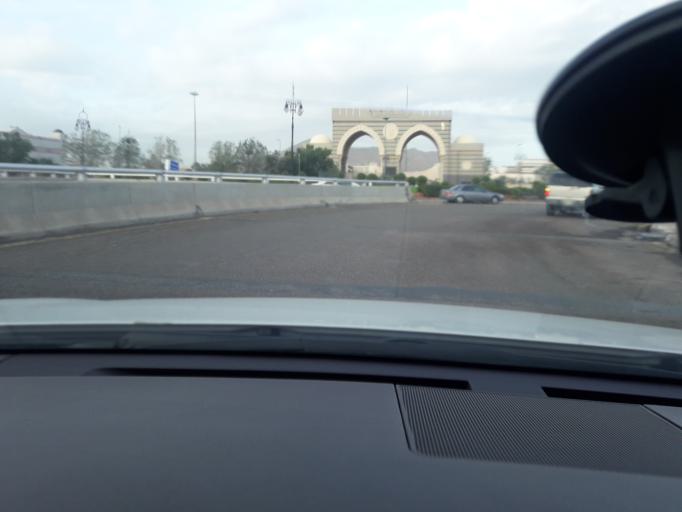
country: SA
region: Al Madinah al Munawwarah
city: Sultanah
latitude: 24.4809
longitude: 39.5673
